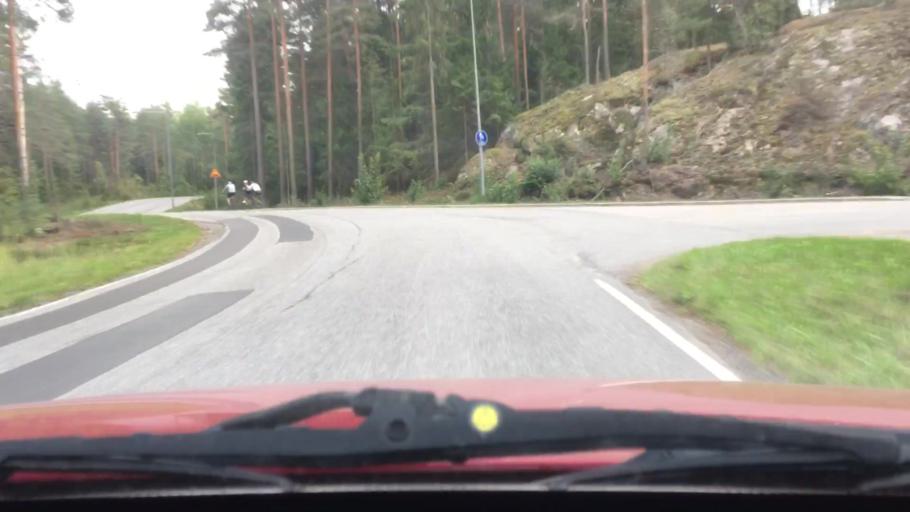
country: FI
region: Varsinais-Suomi
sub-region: Turku
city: Masku
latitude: 60.5533
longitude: 22.1327
